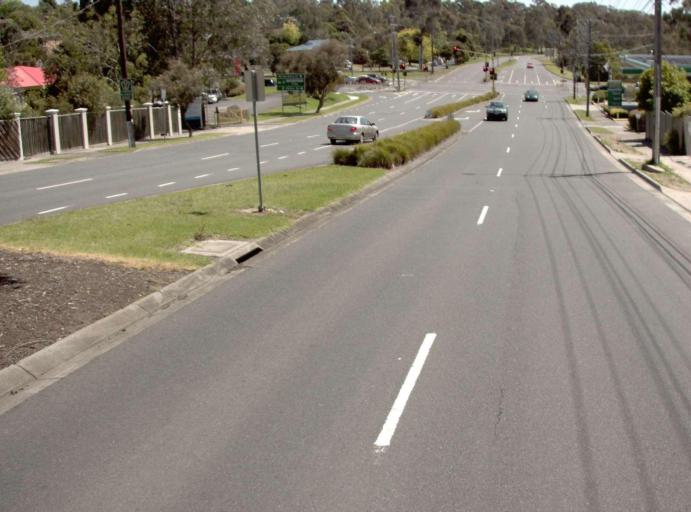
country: AU
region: Victoria
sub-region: Banyule
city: Darch
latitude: -37.7573
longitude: 145.1150
